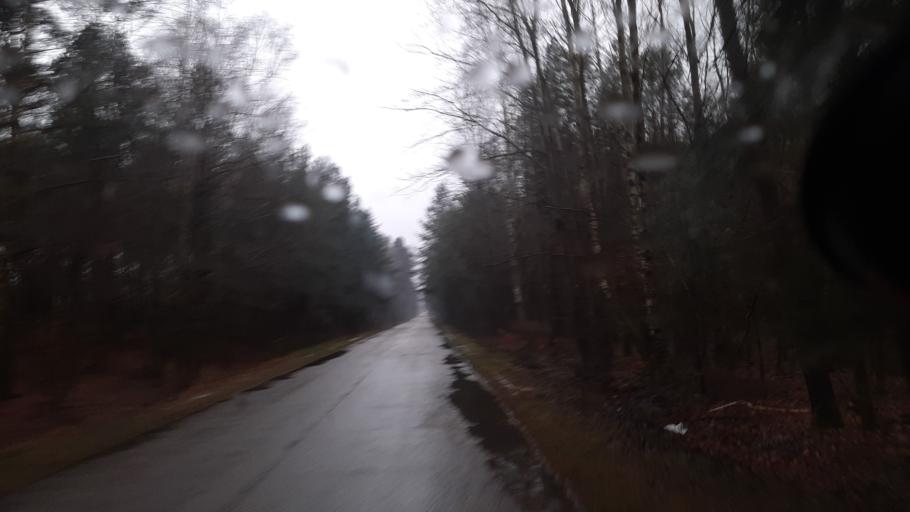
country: PL
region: Lublin Voivodeship
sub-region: Powiat lubartowski
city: Kamionka
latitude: 51.5092
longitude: 22.4903
